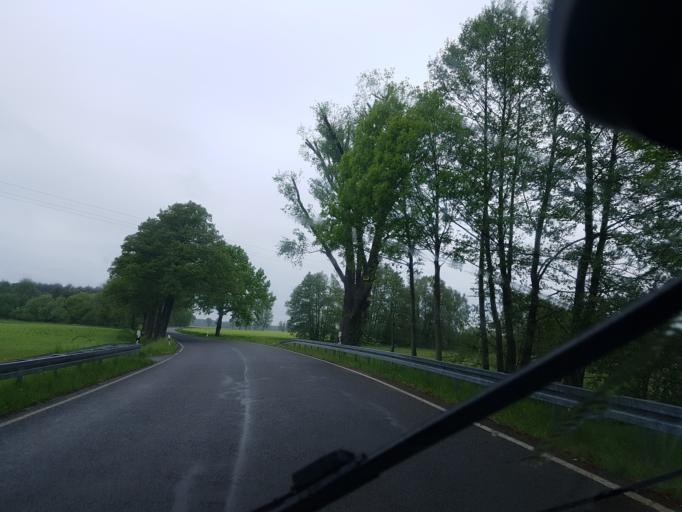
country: DE
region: Brandenburg
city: Spremberg
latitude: 51.6749
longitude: 14.4698
